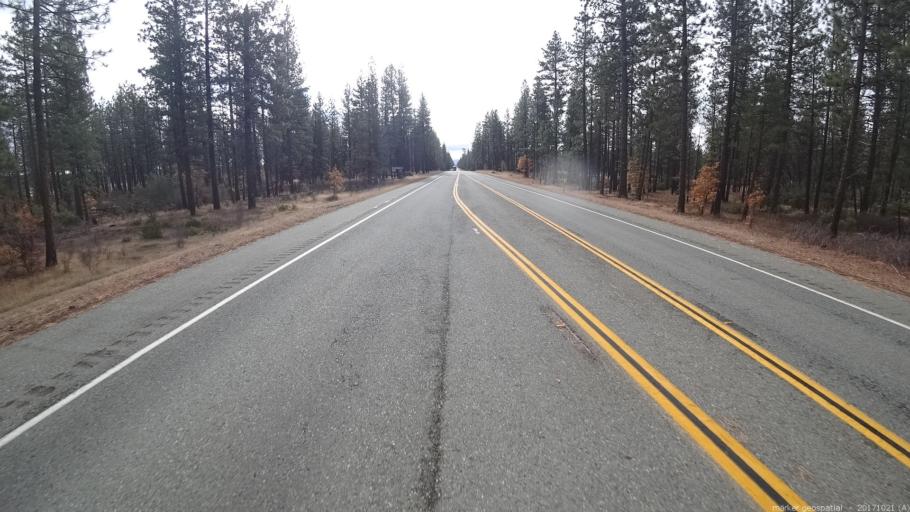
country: US
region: California
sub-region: Shasta County
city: Burney
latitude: 40.9960
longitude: -121.6291
